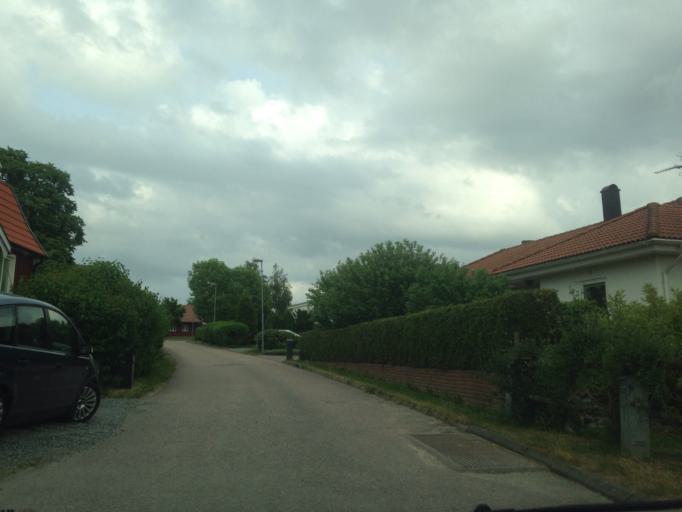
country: SE
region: Vaestra Goetaland
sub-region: Kungalvs Kommun
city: Kungalv
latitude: 57.8052
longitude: 11.9049
